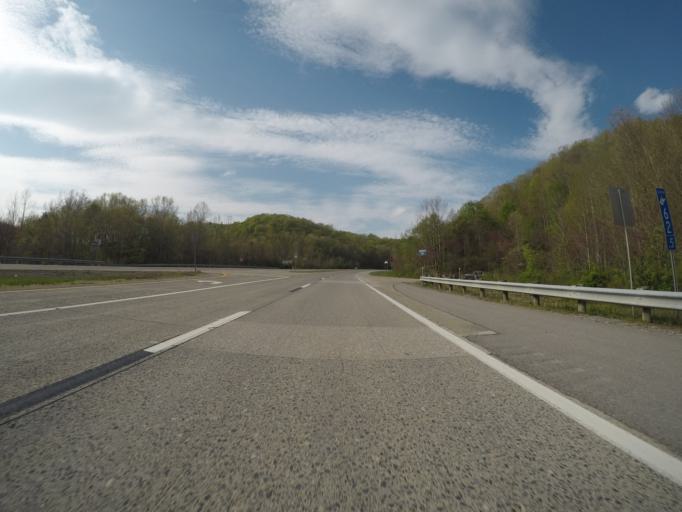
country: US
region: West Virginia
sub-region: Kanawha County
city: Alum Creek
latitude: 38.2069
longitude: -81.8309
